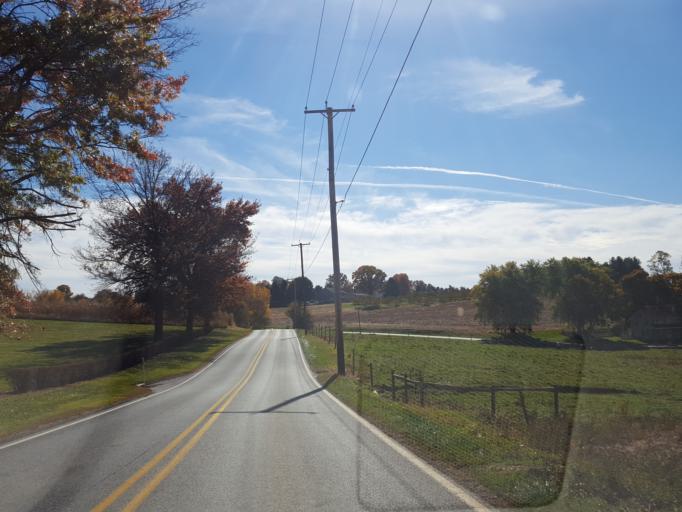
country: US
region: Pennsylvania
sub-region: York County
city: Yoe
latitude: 39.9169
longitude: -76.6576
